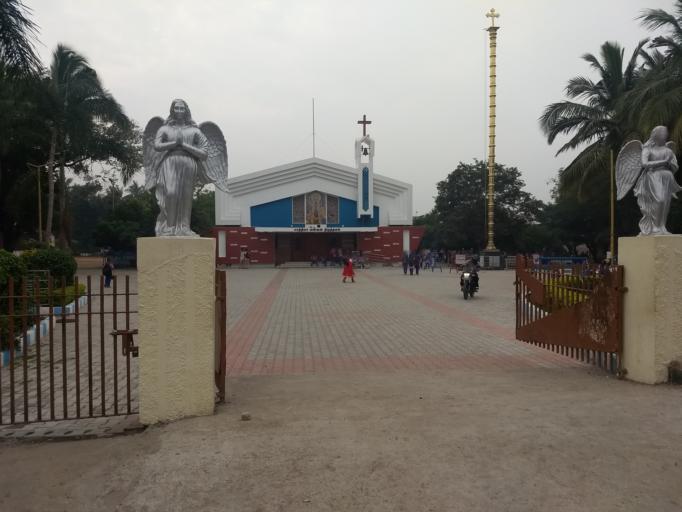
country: IN
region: Tamil Nadu
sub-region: Kancheepuram
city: Vandalur
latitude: 12.9234
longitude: 80.1175
